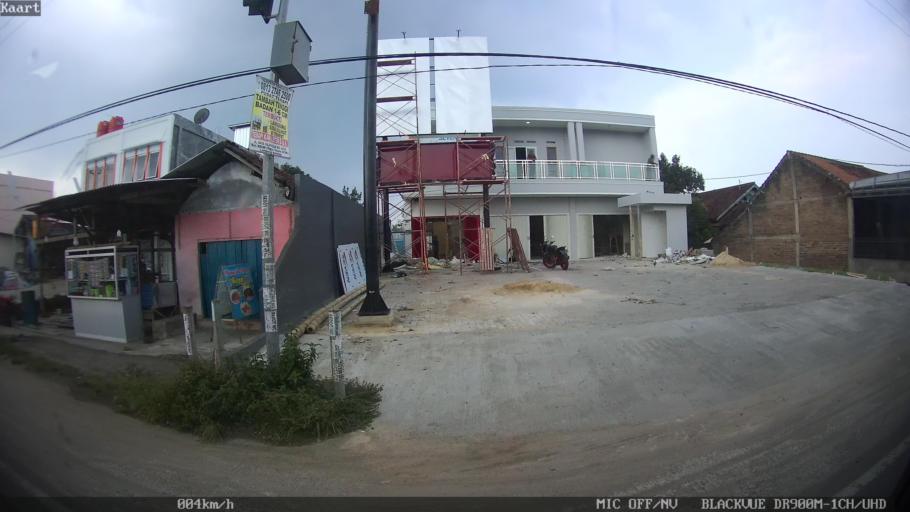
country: ID
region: Lampung
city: Gedongtataan
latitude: -5.3800
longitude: 105.1078
